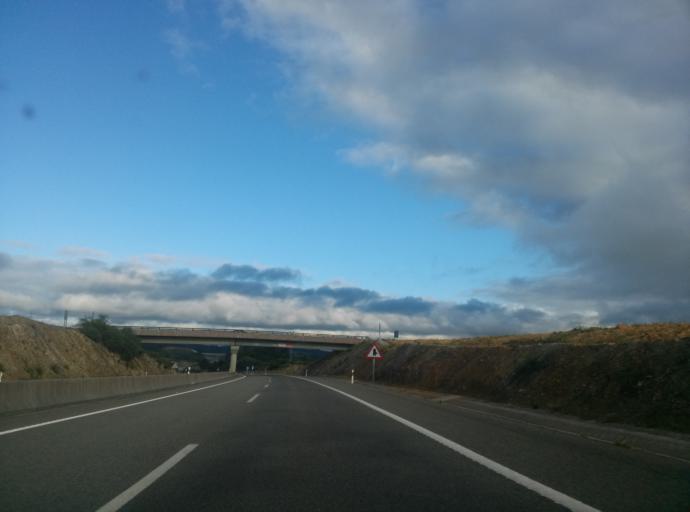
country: ES
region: Galicia
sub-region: Provincia de Lugo
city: Vilalba
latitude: 43.3540
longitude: -7.7464
